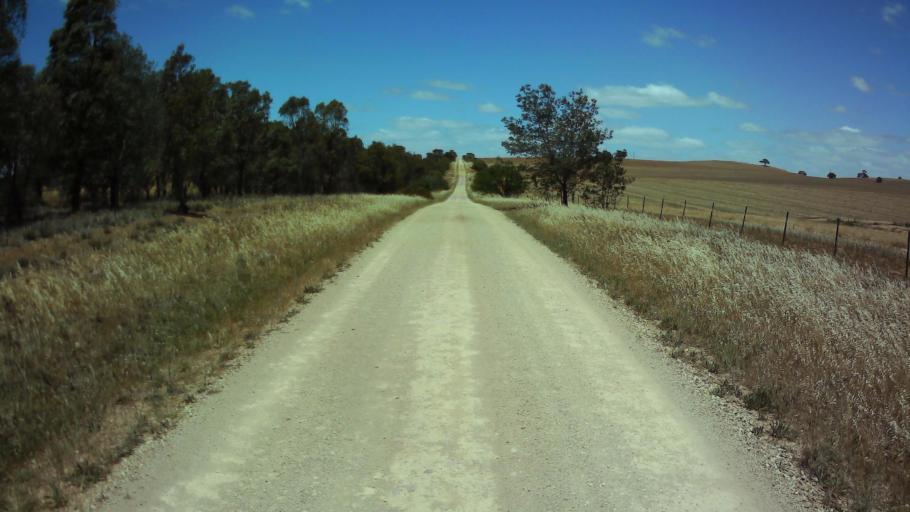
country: AU
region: New South Wales
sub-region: Weddin
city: Grenfell
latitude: -33.9419
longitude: 148.3710
